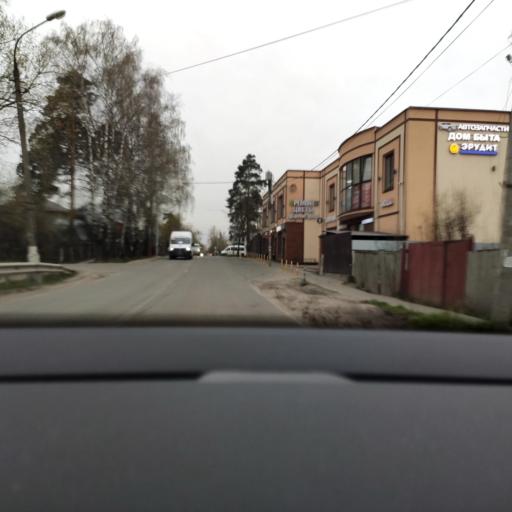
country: RU
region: Moskovskaya
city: Saltykovka
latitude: 55.7747
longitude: 37.8998
